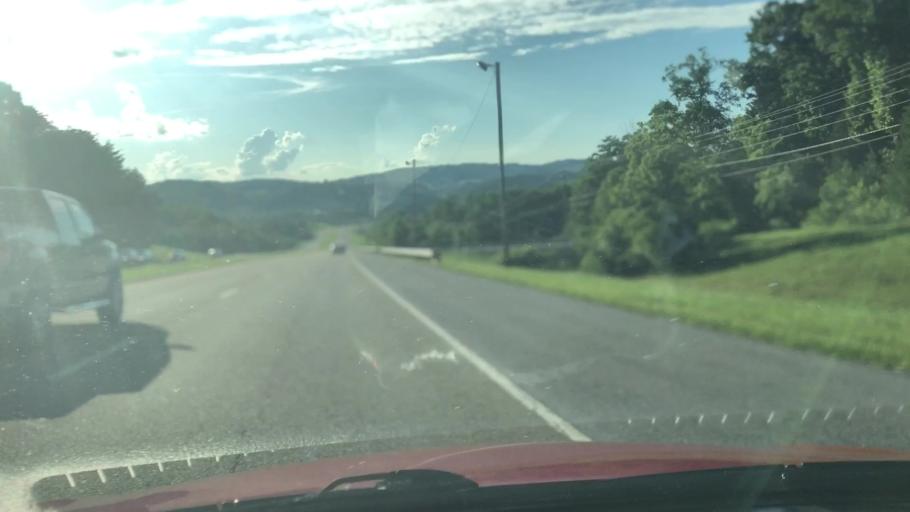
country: US
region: Tennessee
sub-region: Jefferson County
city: Dandridge
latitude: 36.0412
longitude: -83.4470
